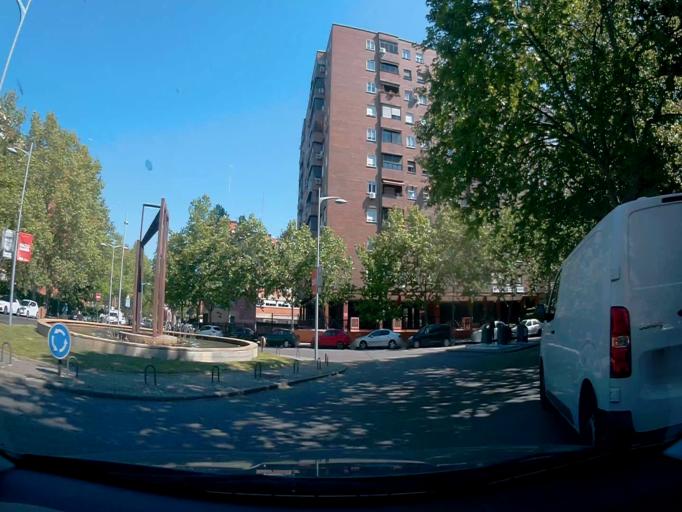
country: ES
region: Madrid
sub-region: Provincia de Madrid
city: Alcorcon
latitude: 40.3433
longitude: -3.8331
